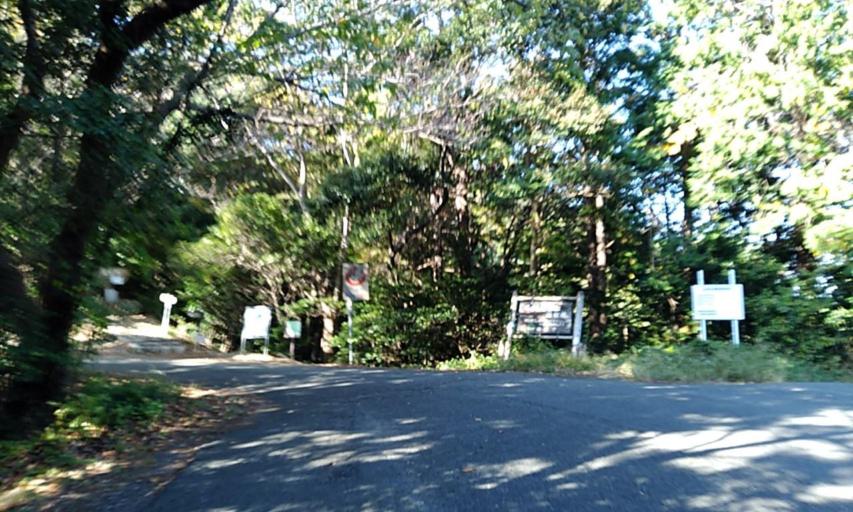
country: JP
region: Shizuoka
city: Hamakita
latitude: 34.8202
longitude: 137.6413
